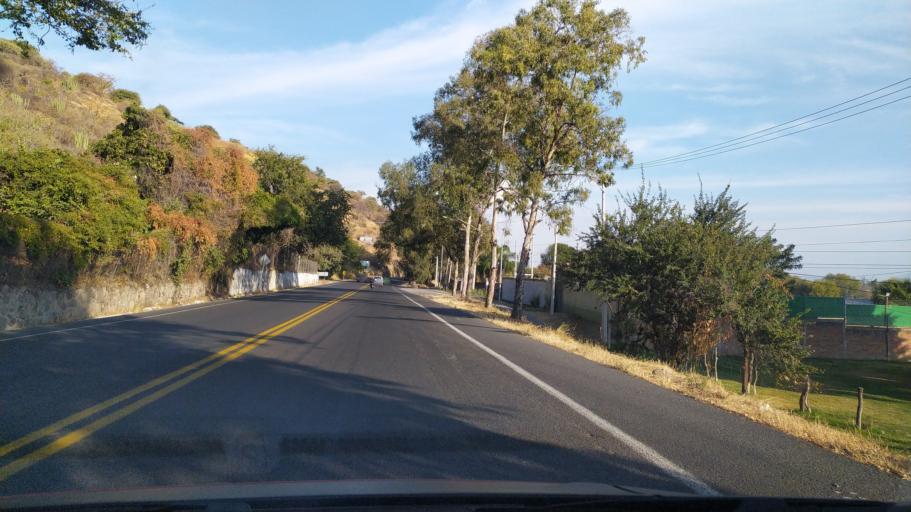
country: MX
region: Jalisco
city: Jamay
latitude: 20.2930
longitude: -102.7281
